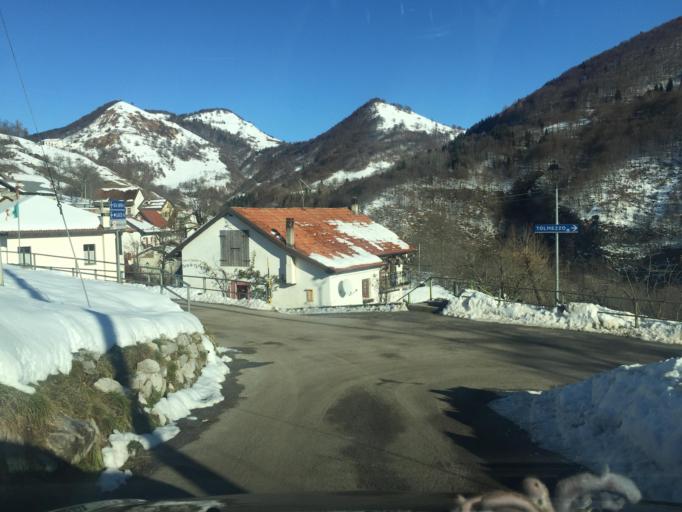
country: IT
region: Friuli Venezia Giulia
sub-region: Provincia di Udine
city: Lauco
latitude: 46.4394
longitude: 12.9682
